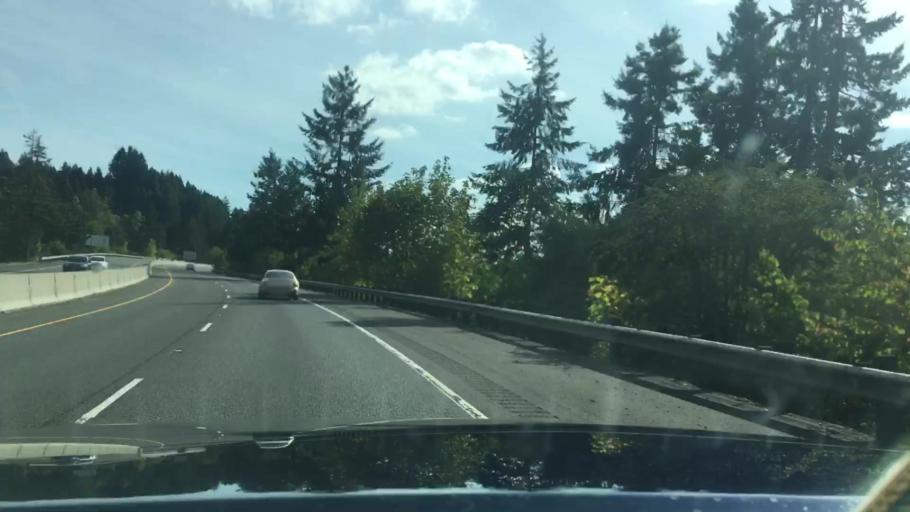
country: US
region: Oregon
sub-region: Lane County
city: Cottage Grove
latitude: 43.7912
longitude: -123.0526
